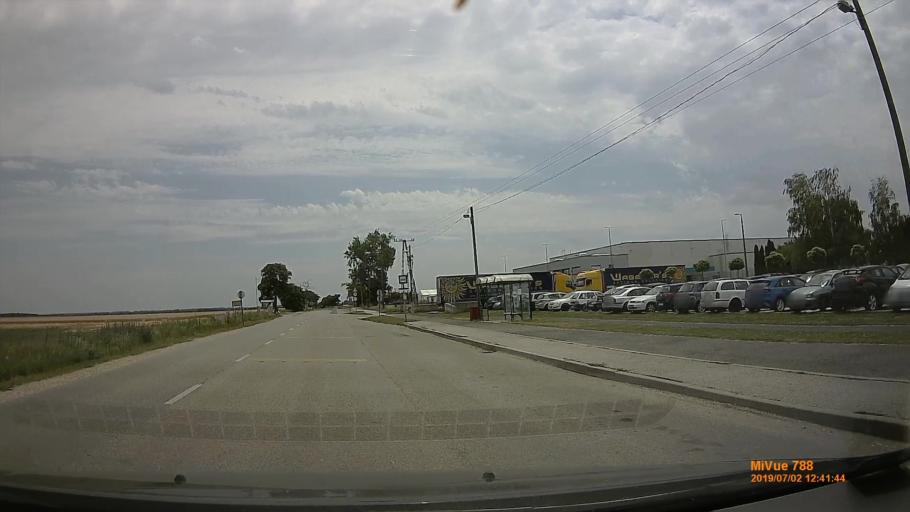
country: HU
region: Gyor-Moson-Sopron
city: Janossomorja
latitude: 47.8483
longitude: 17.1826
